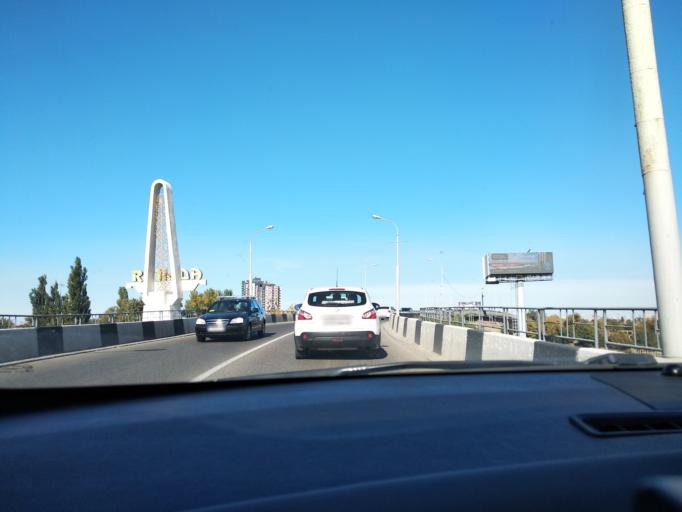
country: RU
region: Adygeya
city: Yablonovskiy
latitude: 44.9939
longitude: 38.9559
